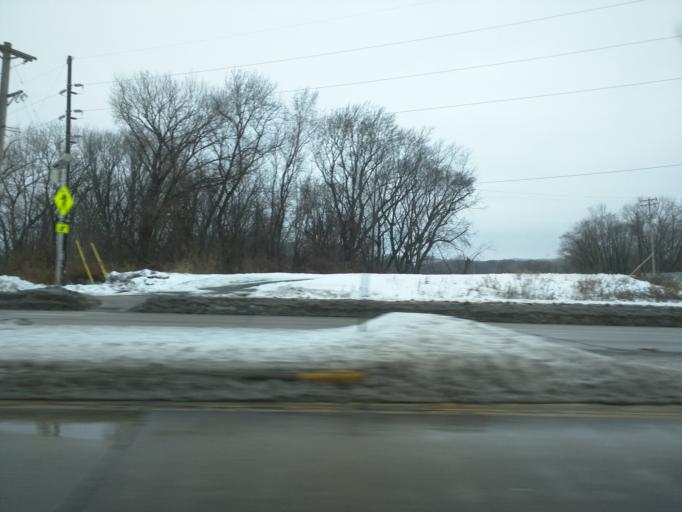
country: US
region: Wisconsin
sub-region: La Crosse County
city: La Crosse
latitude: 43.8204
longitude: -91.2491
